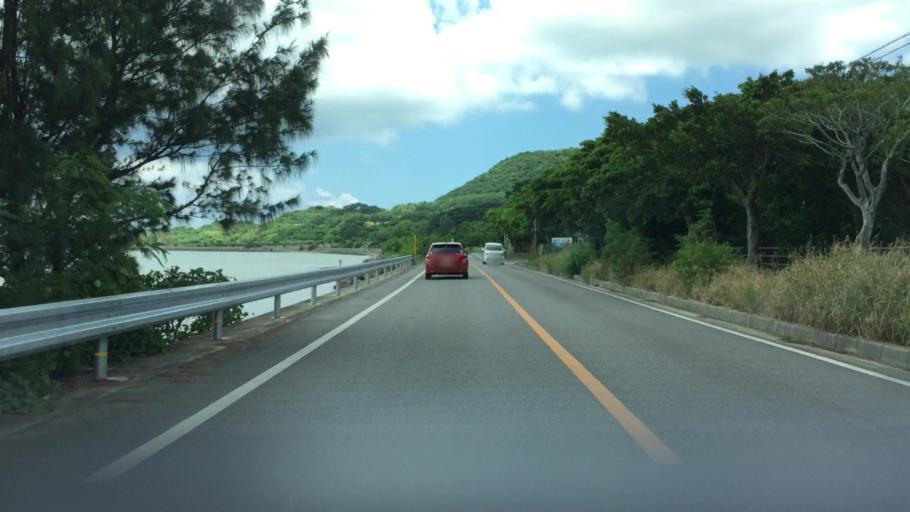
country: JP
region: Okinawa
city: Ishigaki
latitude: 24.4189
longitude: 124.1342
